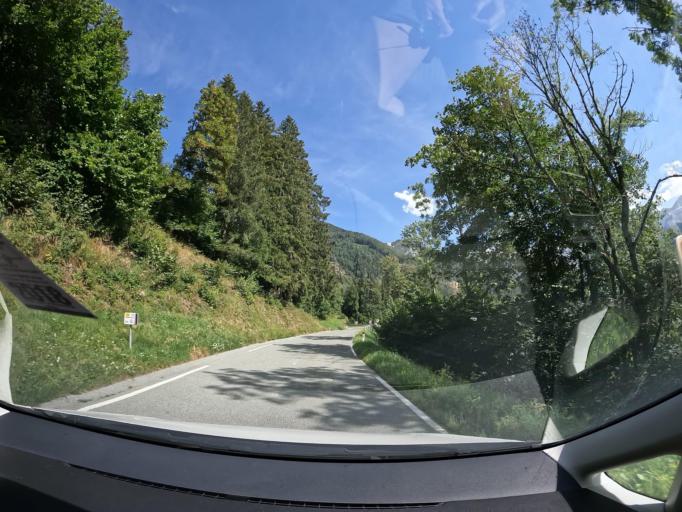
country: AT
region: Carinthia
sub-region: Politischer Bezirk Feldkirchen
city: Glanegg
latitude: 46.7400
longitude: 14.1862
